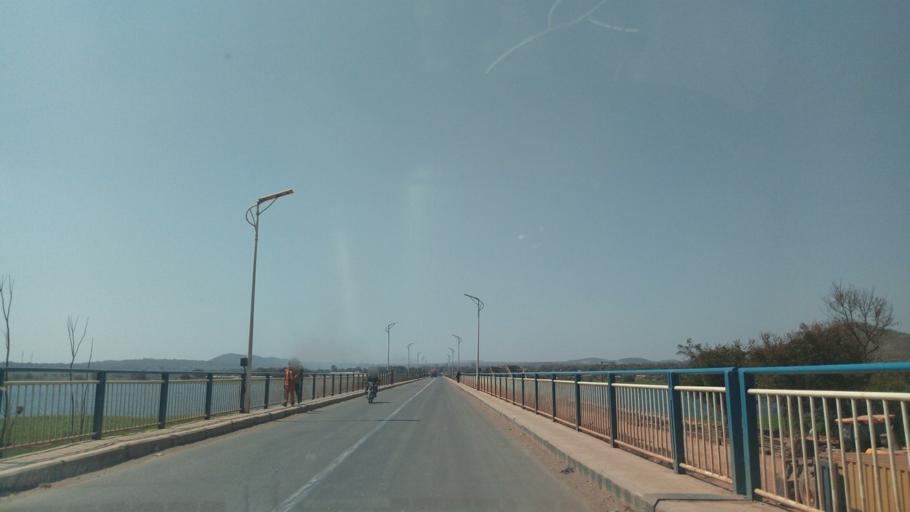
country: CD
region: Katanga
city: Kolwezi
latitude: -10.7814
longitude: 25.7233
